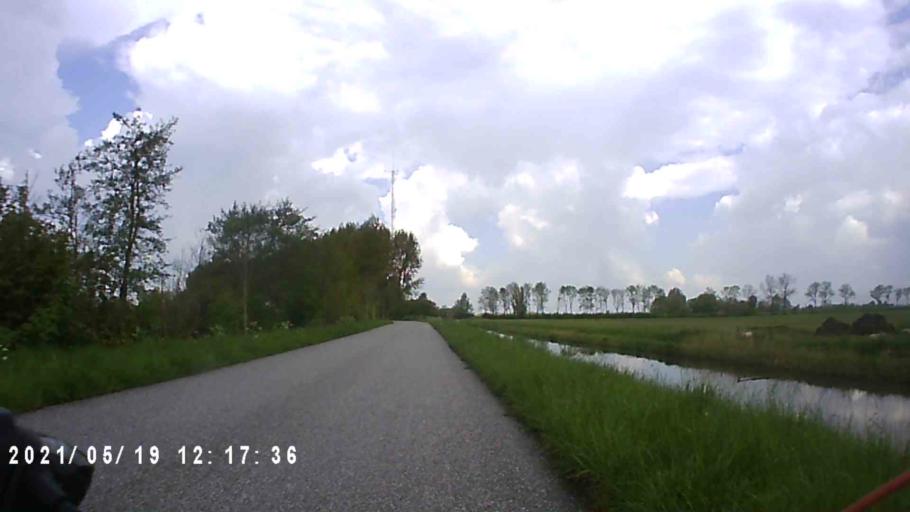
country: NL
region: Friesland
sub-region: Gemeente Kollumerland en Nieuwkruisland
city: Kollum
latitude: 53.2586
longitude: 6.1750
